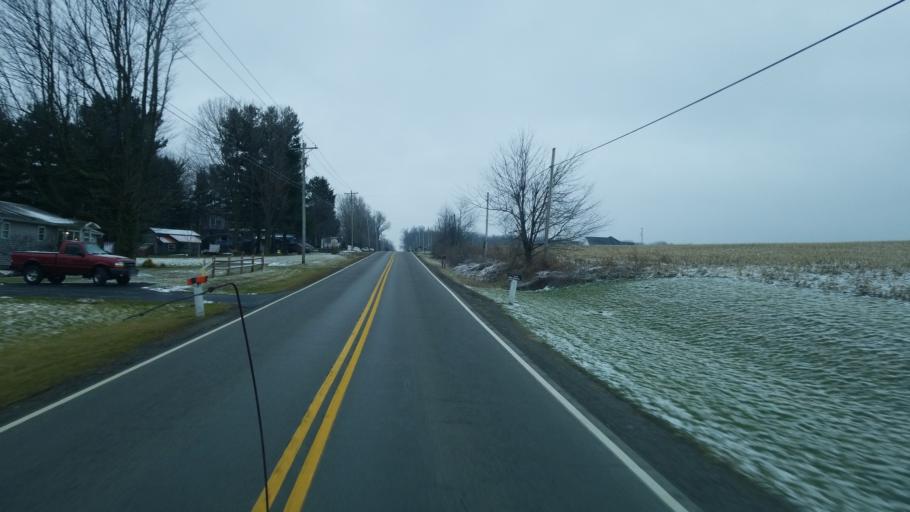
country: US
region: Ohio
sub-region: Wayne County
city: Apple Creek
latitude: 40.7466
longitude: -81.8959
